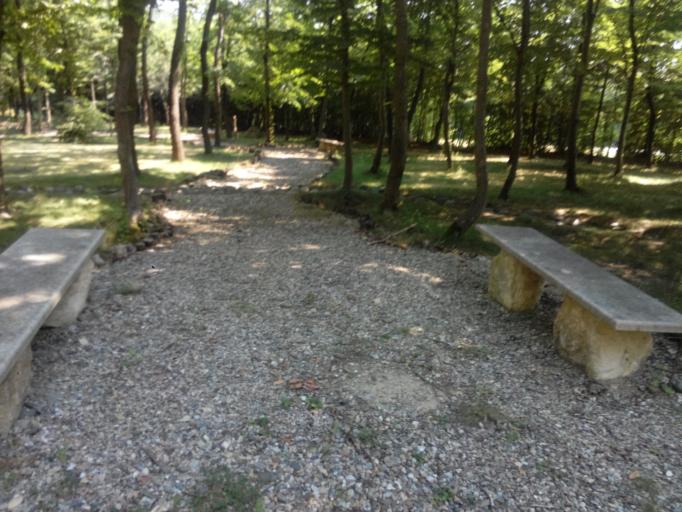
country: RO
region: Cluj
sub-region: Comuna Baciu
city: Baciu
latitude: 46.8102
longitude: 23.4860
